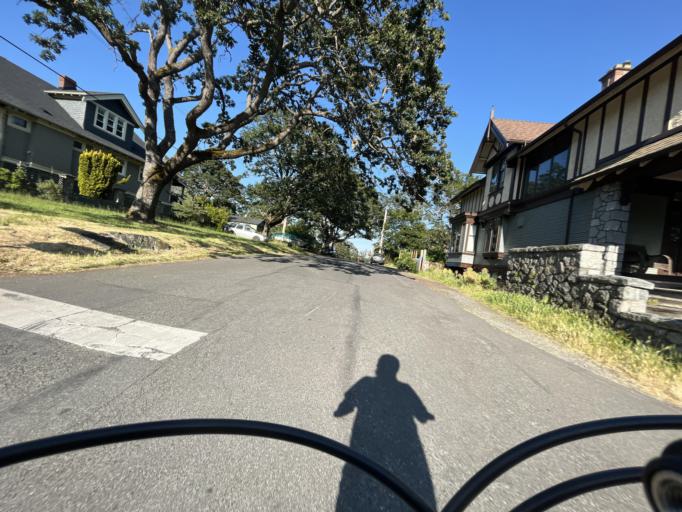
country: CA
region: British Columbia
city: Victoria
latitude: 48.4381
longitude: -123.3448
